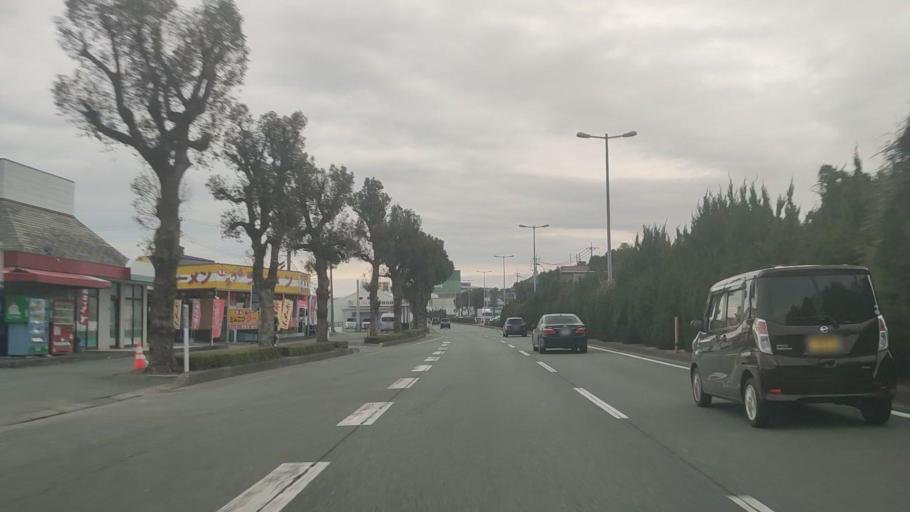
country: JP
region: Kumamoto
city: Kumamoto
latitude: 32.8338
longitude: 130.7757
